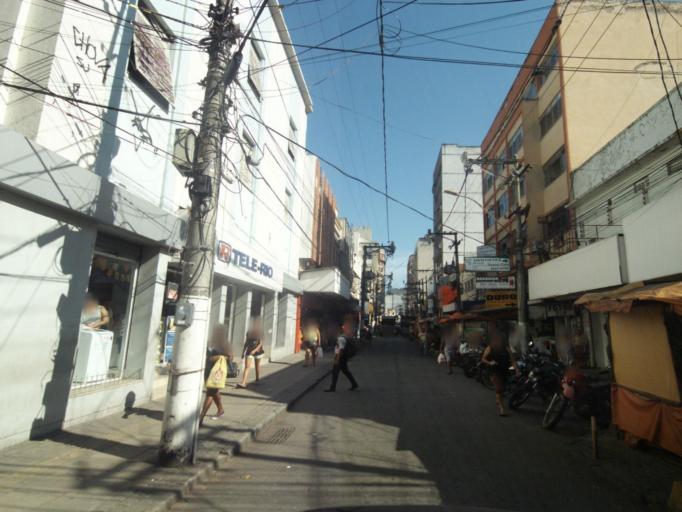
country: BR
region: Rio de Janeiro
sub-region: Niteroi
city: Niteroi
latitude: -22.8920
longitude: -43.1222
